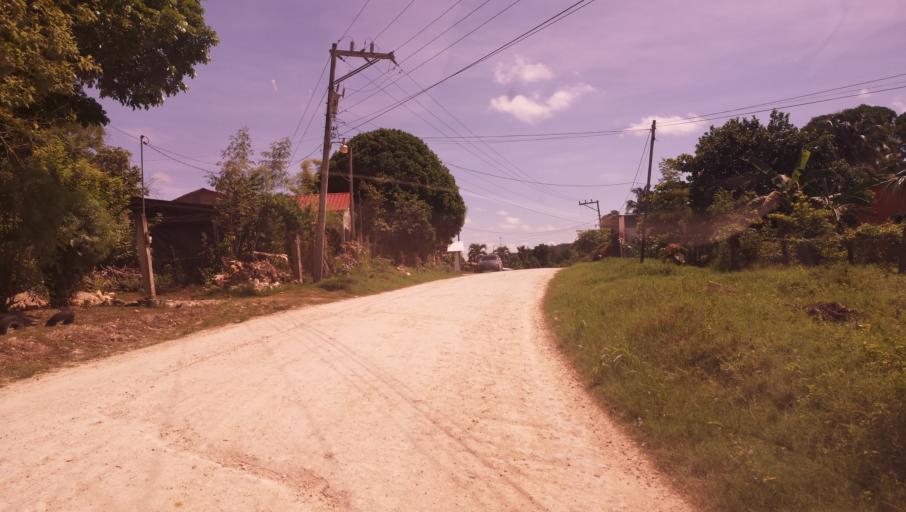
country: GT
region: Peten
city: Melchor de Mencos
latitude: 16.9730
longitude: -89.2650
